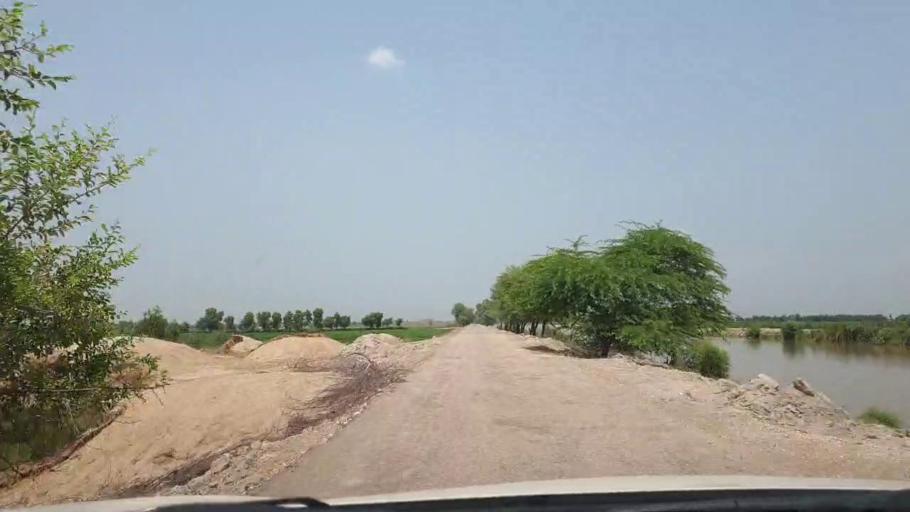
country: PK
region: Sindh
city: Dokri
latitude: 27.3311
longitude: 68.1095
